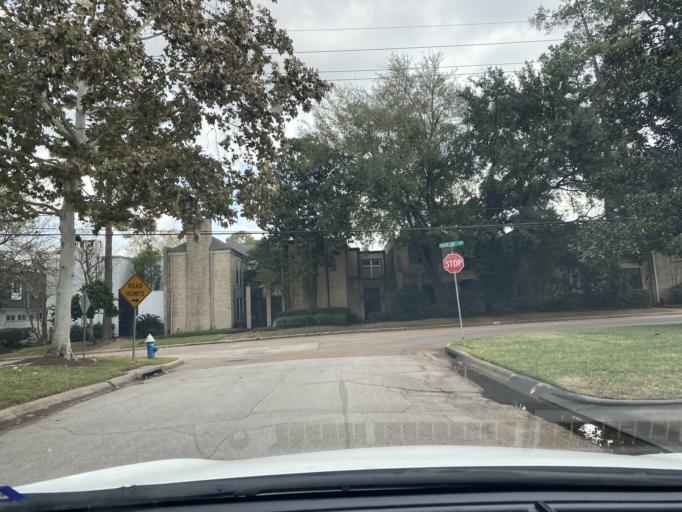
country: US
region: Texas
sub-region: Harris County
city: Hunters Creek Village
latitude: 29.7683
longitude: -95.4680
